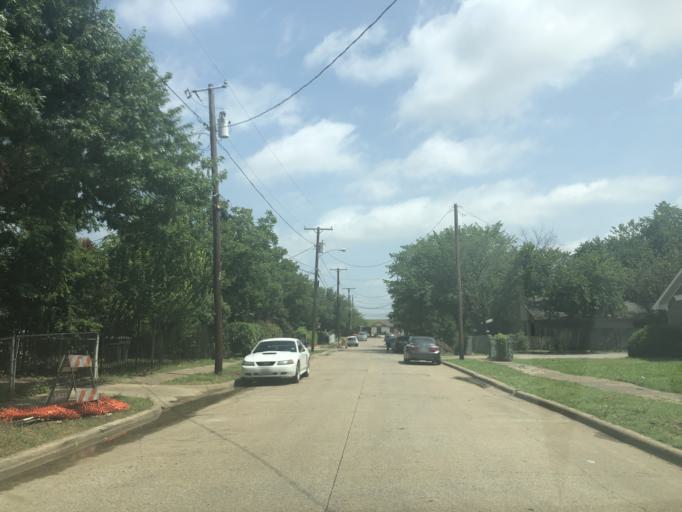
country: US
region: Texas
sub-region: Dallas County
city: Cockrell Hill
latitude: 32.7913
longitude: -96.8802
